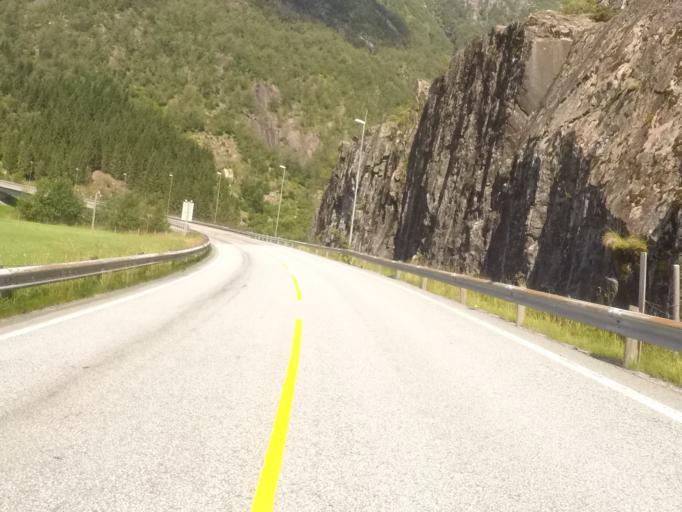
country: NO
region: Hordaland
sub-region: Masfjorden
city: Masfjorden
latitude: 60.9160
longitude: 5.5315
